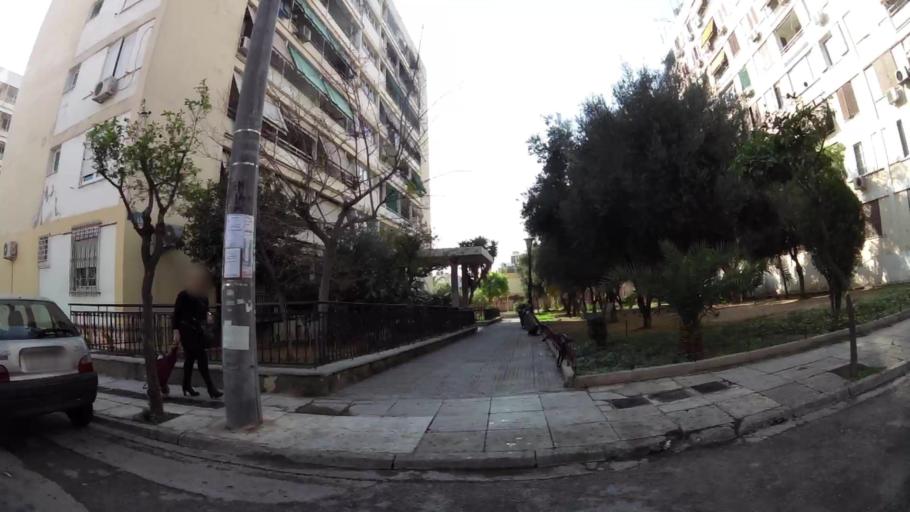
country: GR
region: Attica
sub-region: Nomos Attikis
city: Piraeus
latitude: 37.9491
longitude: 23.6323
